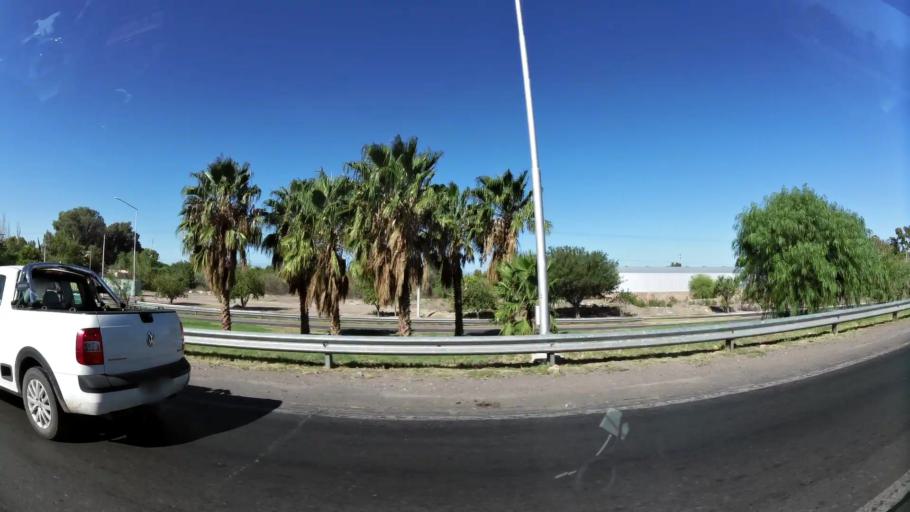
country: AR
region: San Juan
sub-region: Departamento de Santa Lucia
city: Santa Lucia
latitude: -31.5318
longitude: -68.5039
